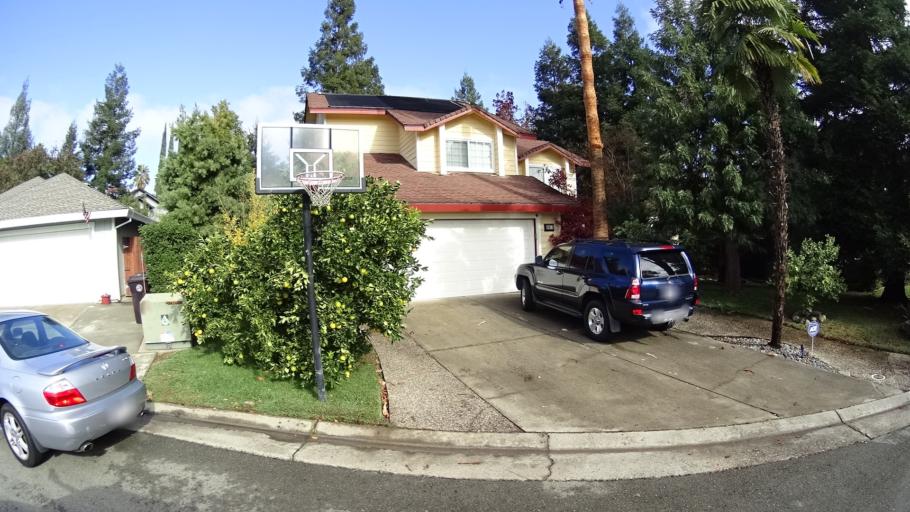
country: US
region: California
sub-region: Sacramento County
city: Antelope
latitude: 38.6872
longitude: -121.3263
